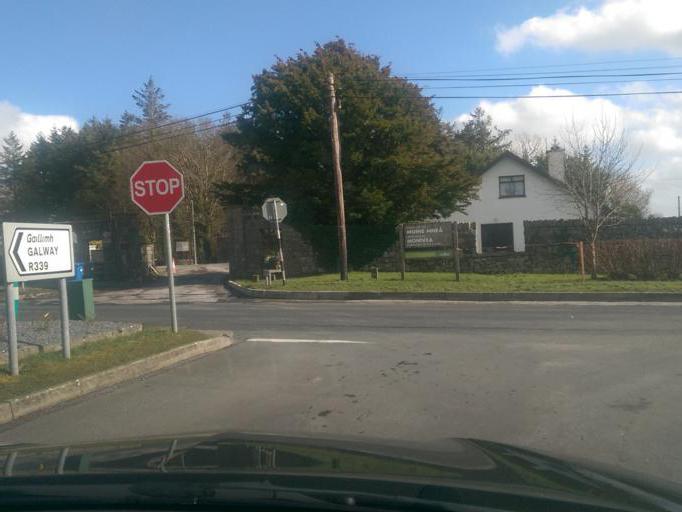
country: IE
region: Connaught
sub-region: County Galway
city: Athenry
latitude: 53.3744
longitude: -8.7010
